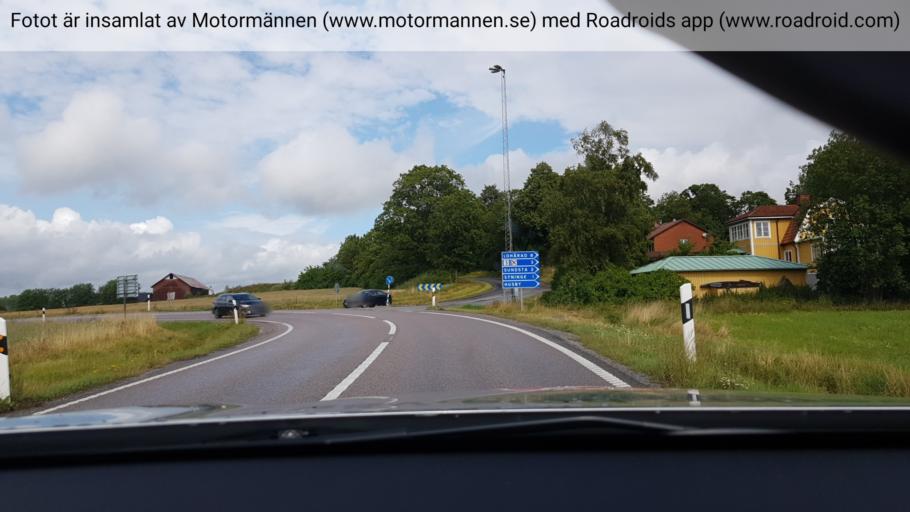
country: SE
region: Stockholm
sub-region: Norrtalje Kommun
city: Rimbo
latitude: 59.7411
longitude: 18.5264
